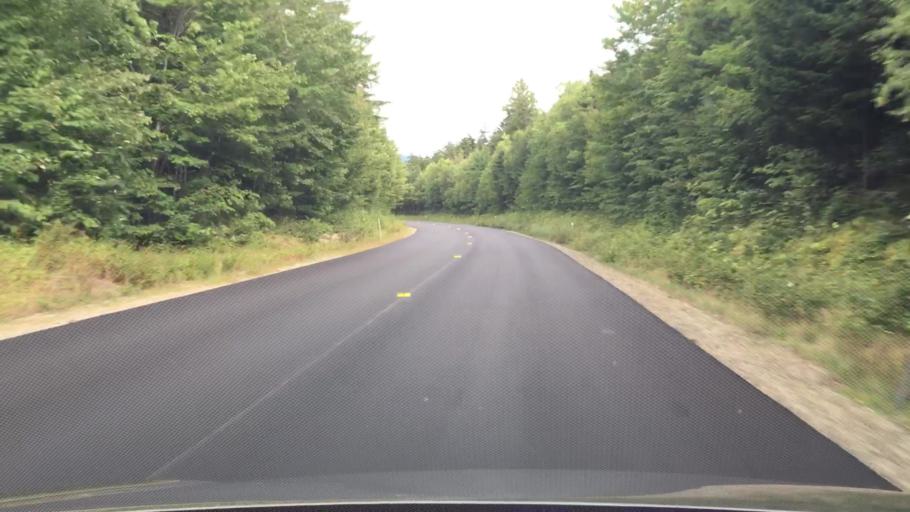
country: US
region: New Hampshire
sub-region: Grafton County
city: Woodstock
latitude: 44.0165
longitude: -71.4596
